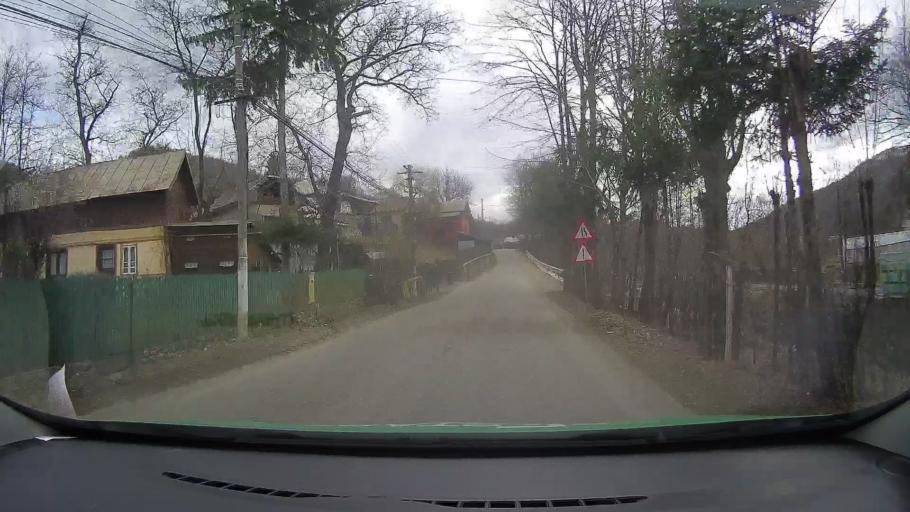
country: RO
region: Dambovita
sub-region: Comuna Visinesti
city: Visinesti
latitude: 45.1037
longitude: 25.5599
